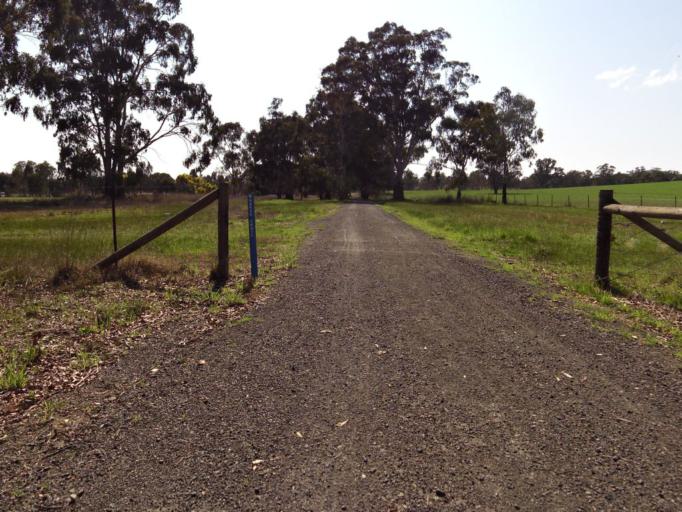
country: AU
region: Victoria
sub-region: Murrindindi
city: Alexandra
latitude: -37.1240
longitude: 145.5998
